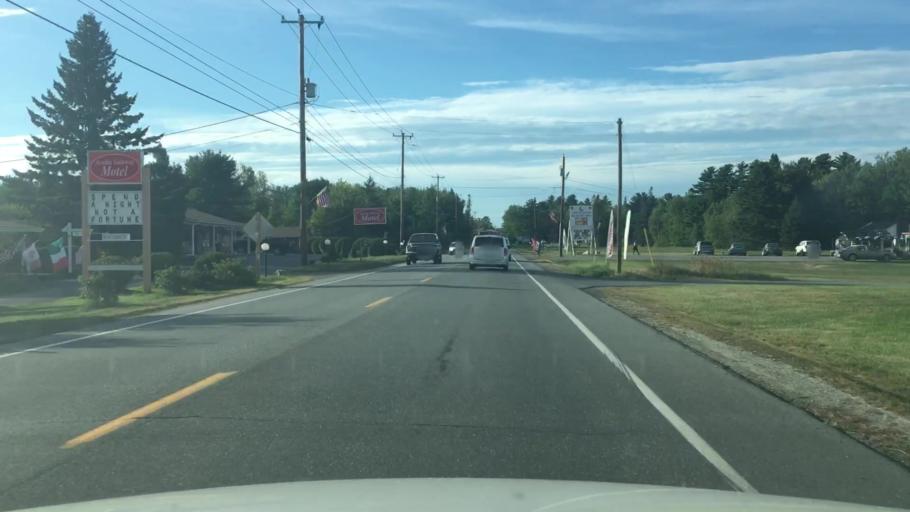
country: US
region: Maine
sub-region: Hancock County
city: Trenton
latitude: 44.4908
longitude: -68.3731
